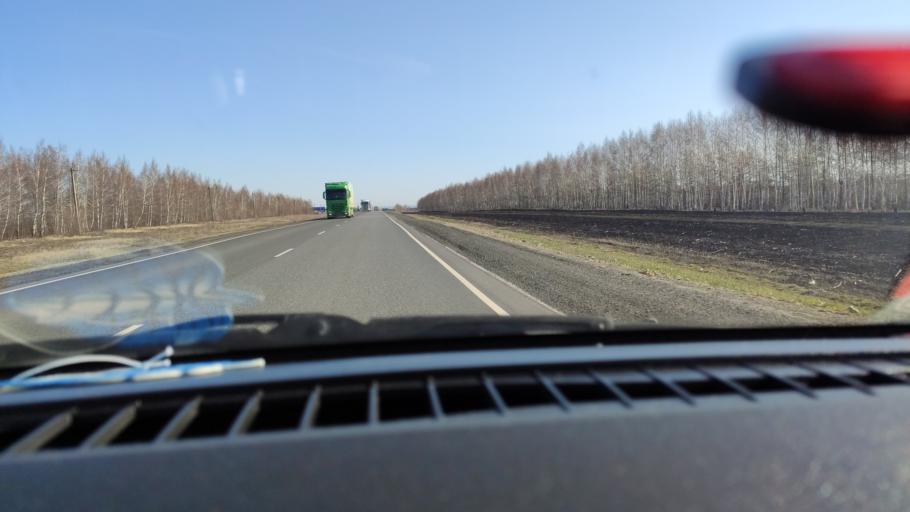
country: RU
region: Samara
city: Syzran'
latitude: 52.9917
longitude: 48.3220
